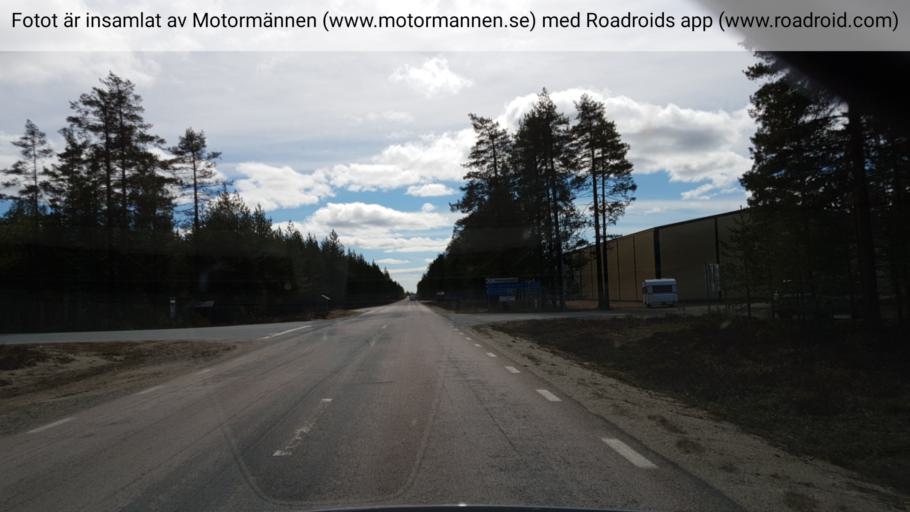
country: SE
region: Vaesternorrland
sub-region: OErnskoeldsviks Kommun
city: Husum
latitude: 63.4594
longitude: 18.9568
